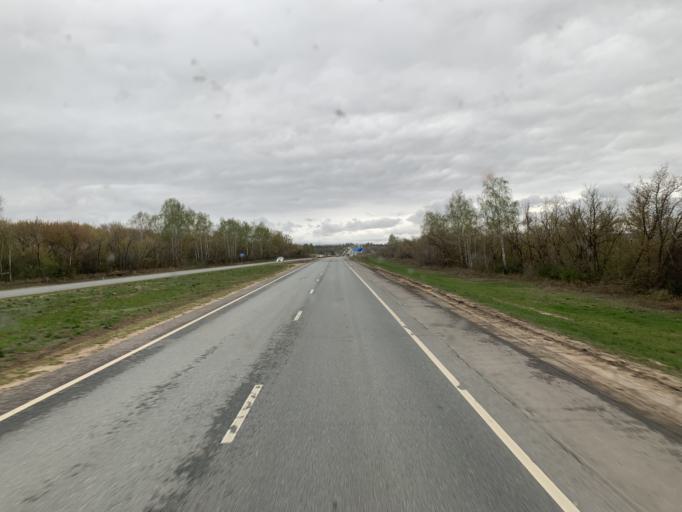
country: RU
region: Ulyanovsk
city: Kanadey
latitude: 53.1478
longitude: 47.5685
